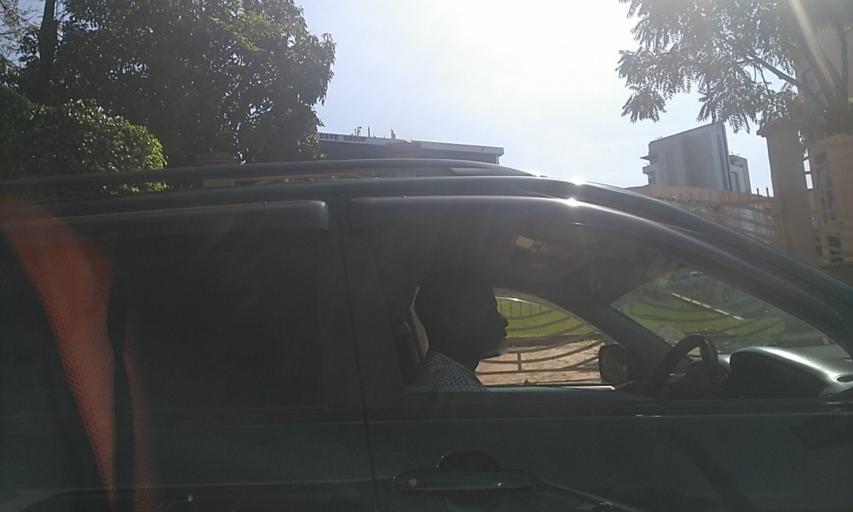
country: UG
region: Central Region
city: Kampala Central Division
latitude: 0.3322
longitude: 32.5791
